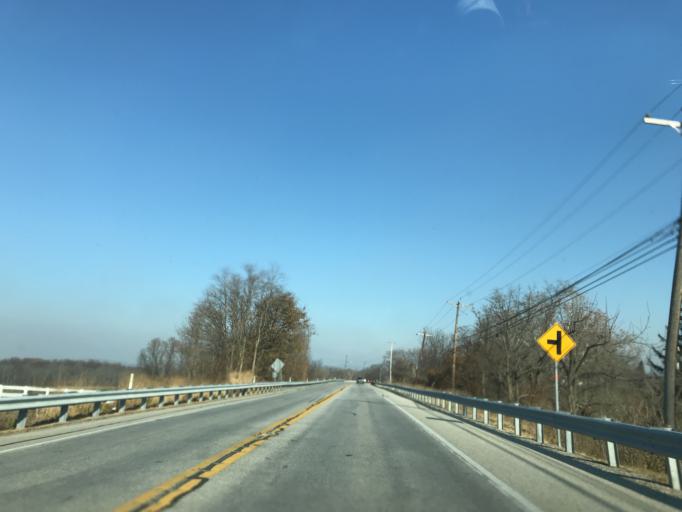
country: US
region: Pennsylvania
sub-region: York County
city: Pennville
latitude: 39.7581
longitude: -77.0339
